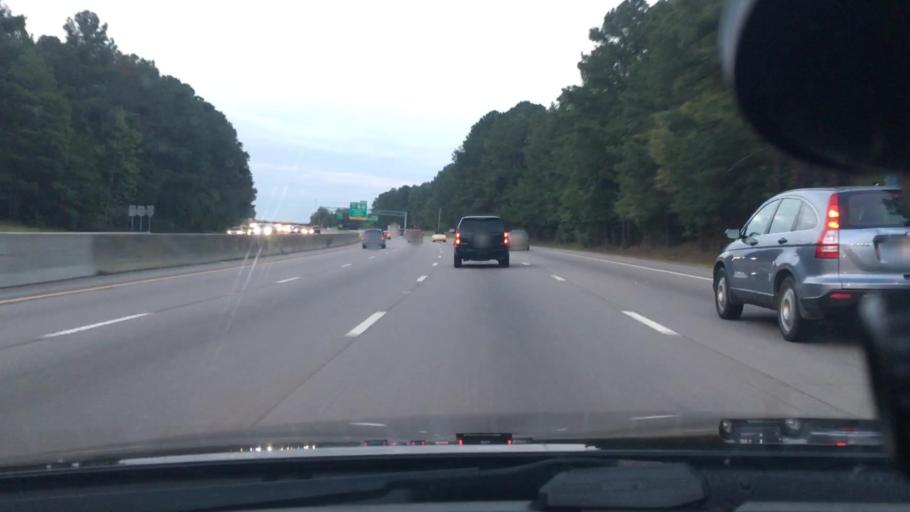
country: US
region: North Carolina
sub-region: Wake County
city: Garner
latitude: 35.7608
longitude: -78.5749
